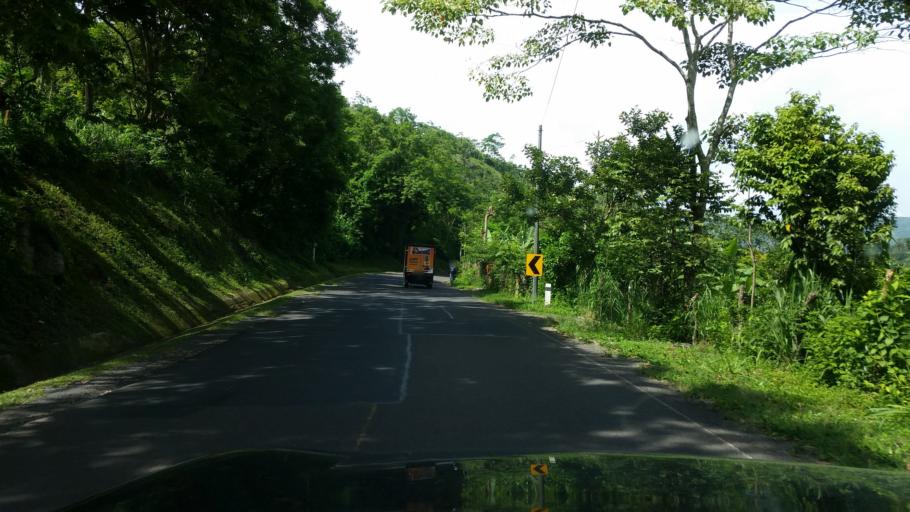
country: NI
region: Matagalpa
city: San Ramon
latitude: 12.9927
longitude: -85.8259
